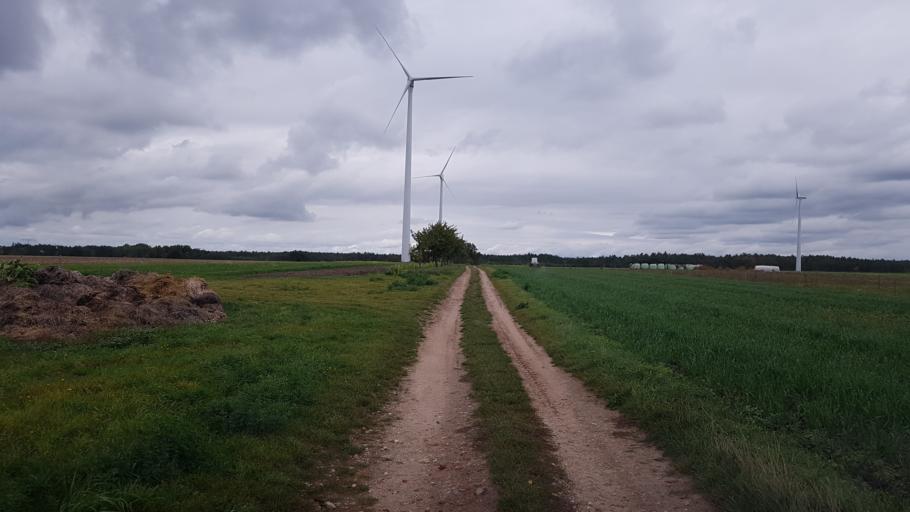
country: DE
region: Brandenburg
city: Doberlug-Kirchhain
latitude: 51.6170
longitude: 13.5934
